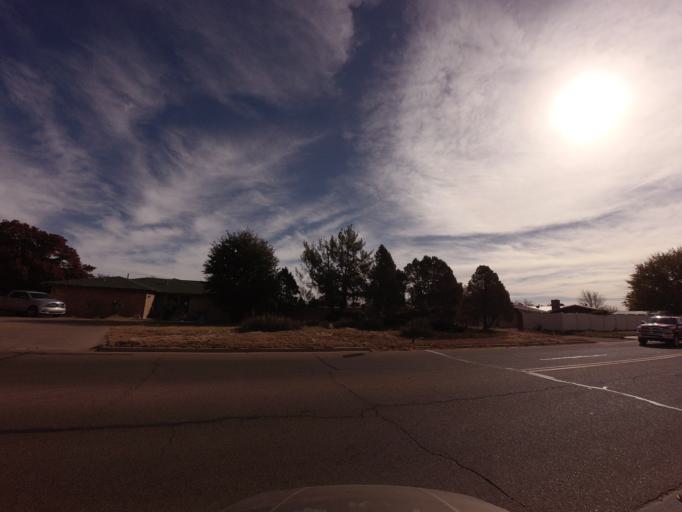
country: US
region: New Mexico
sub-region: Curry County
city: Clovis
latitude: 34.4161
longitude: -103.1877
